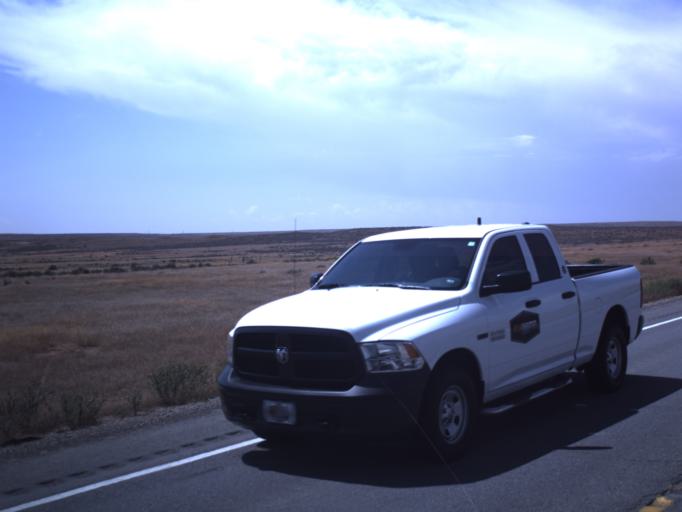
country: US
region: Utah
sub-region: Uintah County
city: Maeser
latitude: 40.3299
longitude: -109.6625
